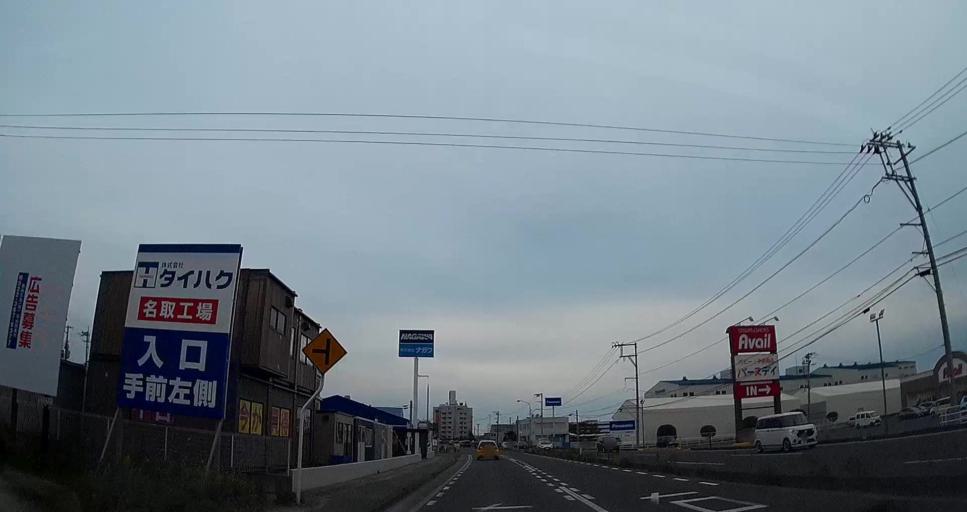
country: JP
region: Miyagi
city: Iwanuma
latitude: 38.1595
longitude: 140.8888
